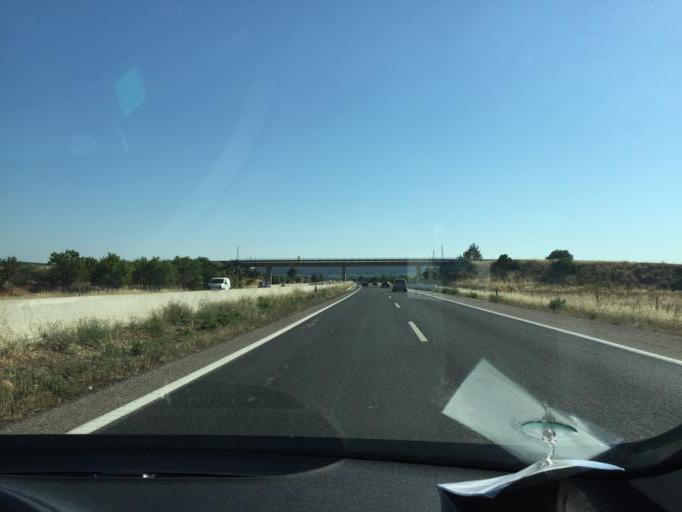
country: ES
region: Balearic Islands
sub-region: Illes Balears
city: Consell
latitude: 39.6578
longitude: 2.8048
